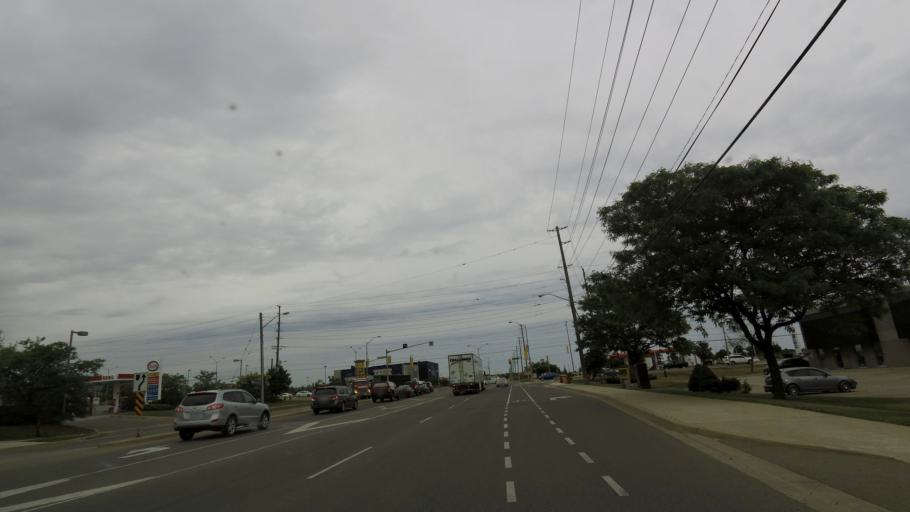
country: CA
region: Ontario
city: Burlington
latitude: 43.3912
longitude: -79.7528
